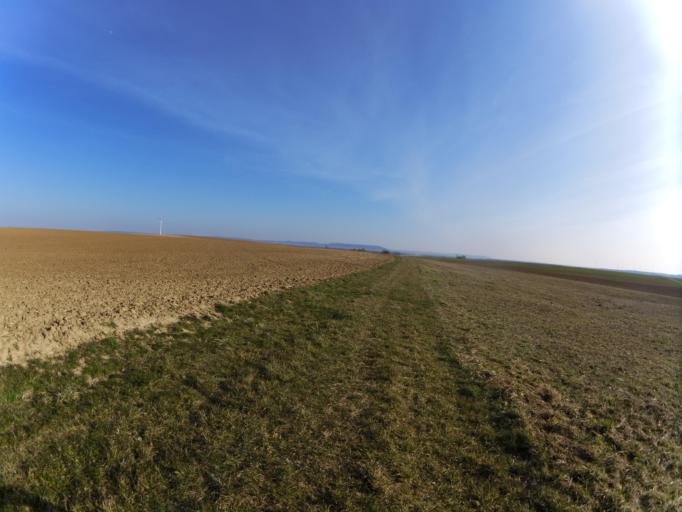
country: DE
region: Bavaria
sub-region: Regierungsbezirk Unterfranken
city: Prosselsheim
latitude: 49.8375
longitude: 10.1220
